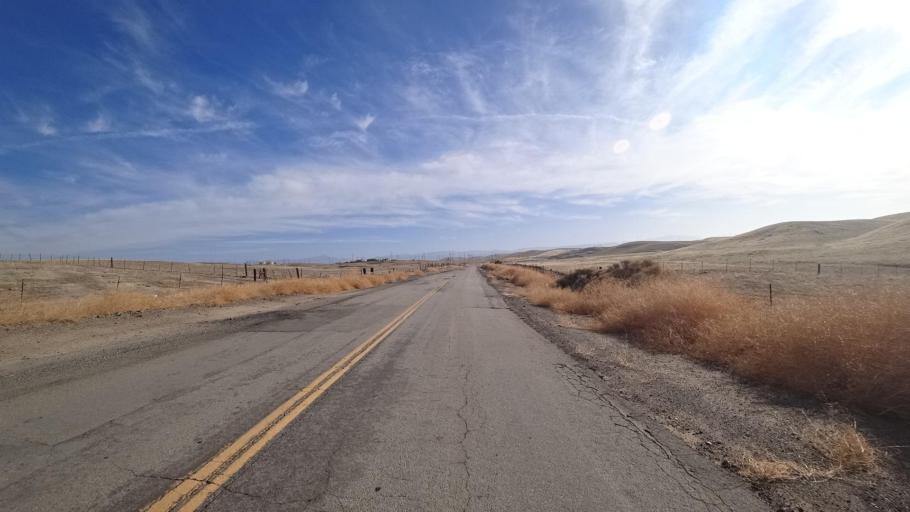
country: US
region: California
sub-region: Tulare County
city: Richgrove
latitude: 35.6263
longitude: -118.9941
